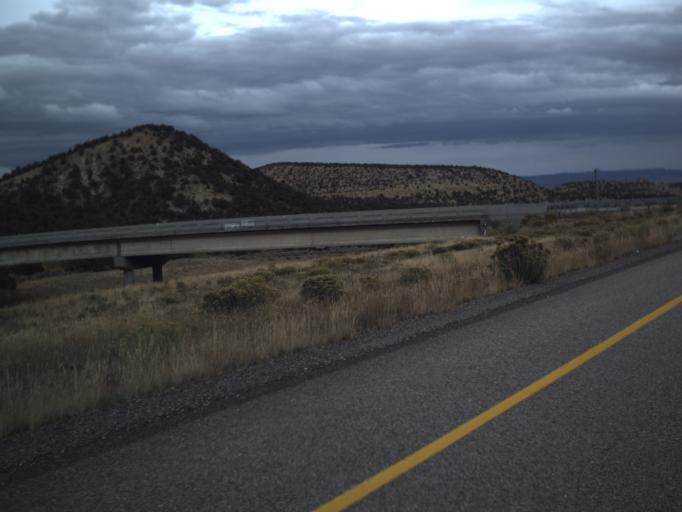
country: US
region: Utah
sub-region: Wayne County
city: Loa
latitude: 38.7565
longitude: -111.4267
